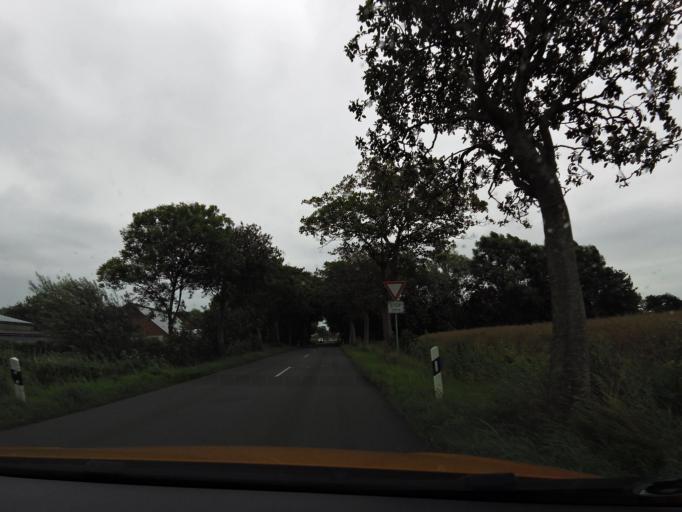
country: DE
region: Lower Saxony
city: Wirdum
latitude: 53.5036
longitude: 7.1965
